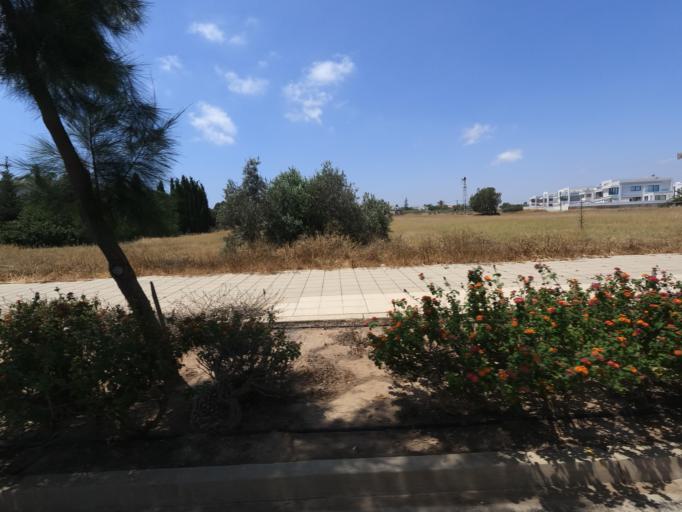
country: CY
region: Ammochostos
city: Protaras
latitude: 35.0334
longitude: 34.0273
